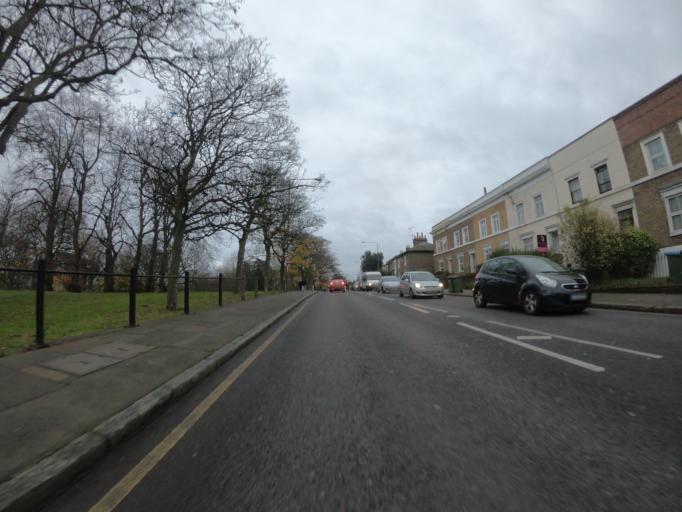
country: GB
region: England
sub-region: Greater London
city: Woolwich
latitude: 51.4815
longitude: 0.0747
